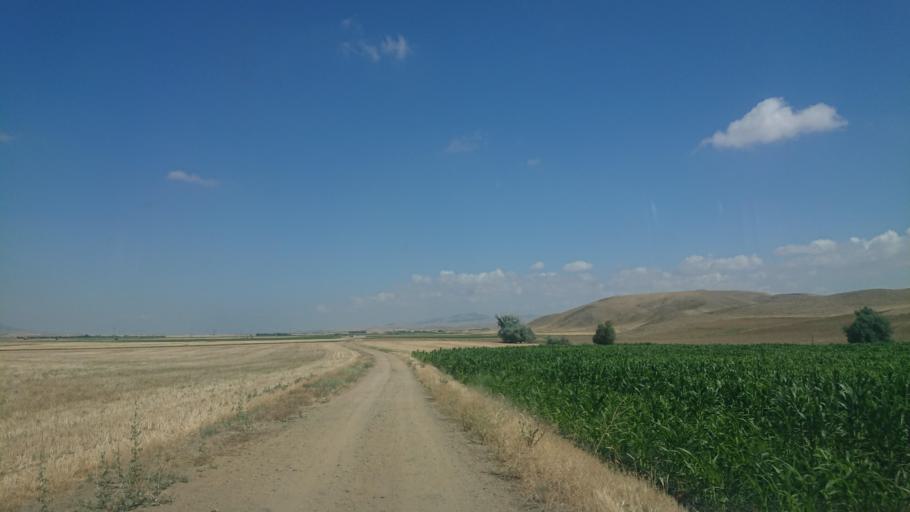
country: TR
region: Aksaray
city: Sariyahsi
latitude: 38.9698
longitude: 33.9189
